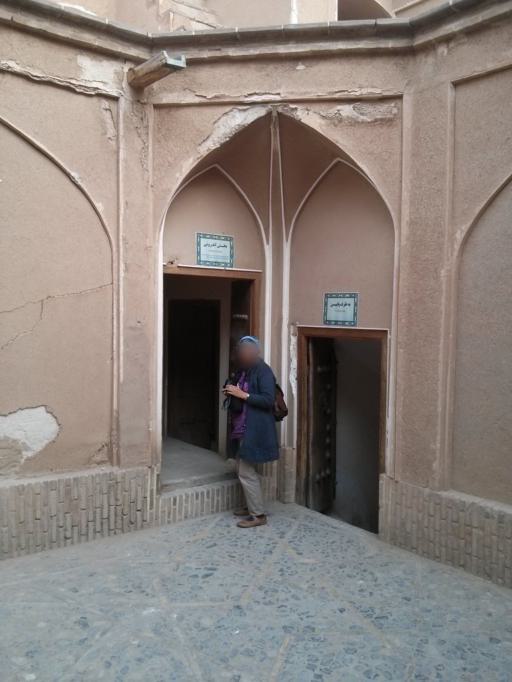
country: IR
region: Isfahan
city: Kashan
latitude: 33.9759
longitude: 51.4409
